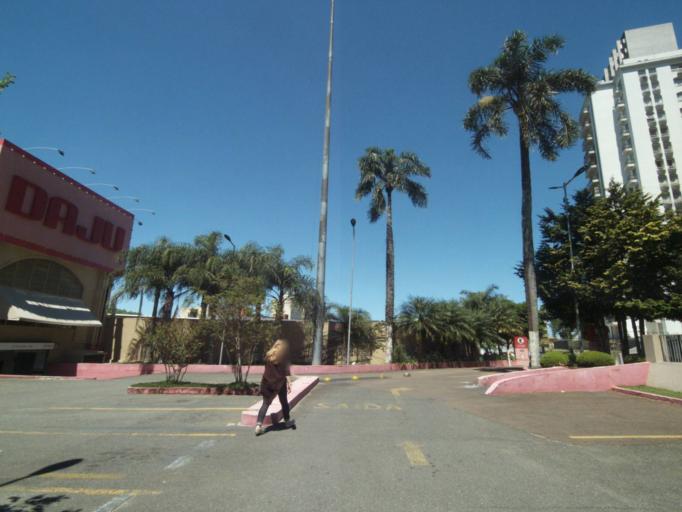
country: BR
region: Parana
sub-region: Curitiba
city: Curitiba
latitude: -25.4106
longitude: -49.2552
